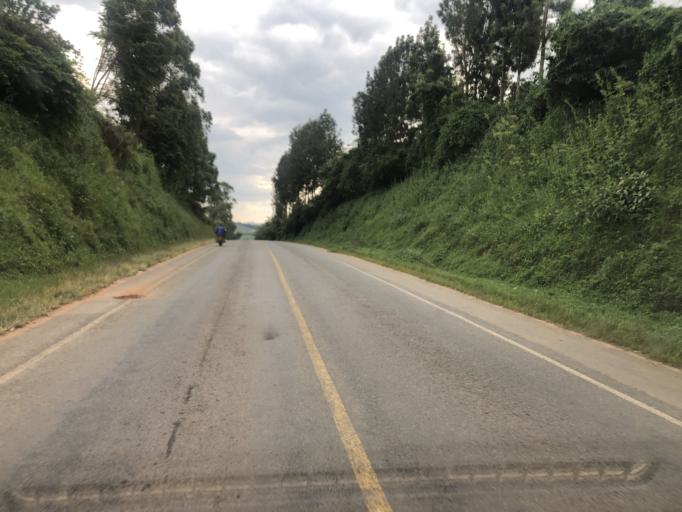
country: UG
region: Western Region
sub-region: Sheema District
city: Kibingo
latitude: -0.5617
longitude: 30.3376
